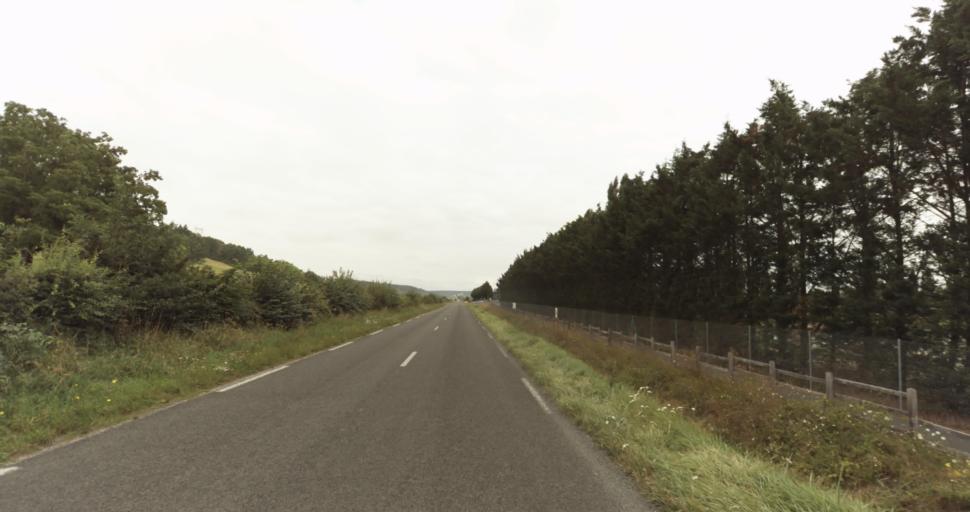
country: FR
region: Haute-Normandie
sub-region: Departement de l'Eure
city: Ivry-la-Bataille
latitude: 48.8985
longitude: 1.4534
